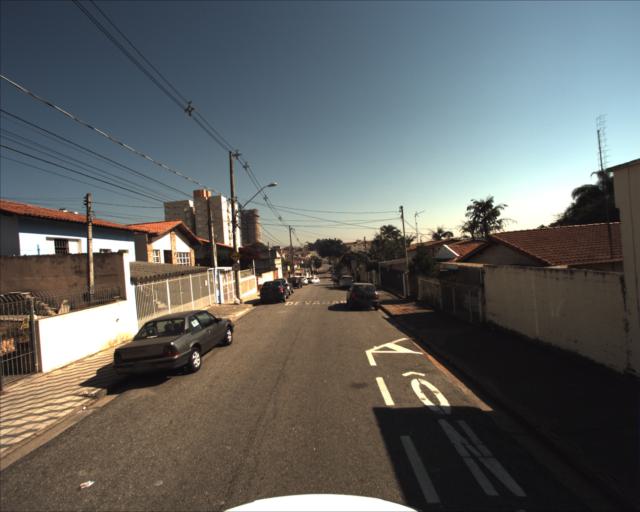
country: BR
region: Sao Paulo
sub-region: Sorocaba
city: Sorocaba
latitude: -23.5063
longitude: -47.4392
